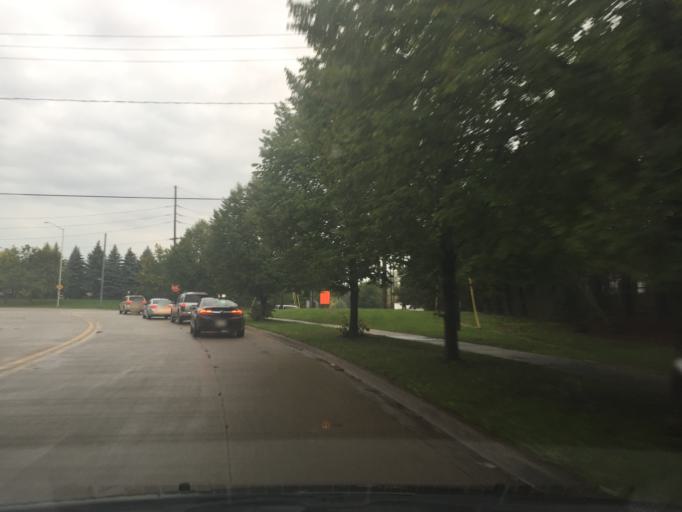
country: US
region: Michigan
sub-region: Oakland County
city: Pontiac
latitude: 42.6250
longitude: -83.2884
